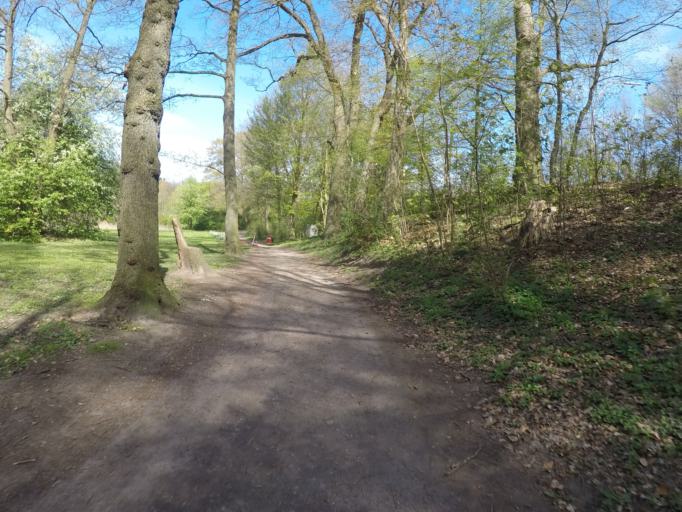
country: DE
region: Hamburg
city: Poppenbuettel
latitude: 53.6551
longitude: 10.0873
